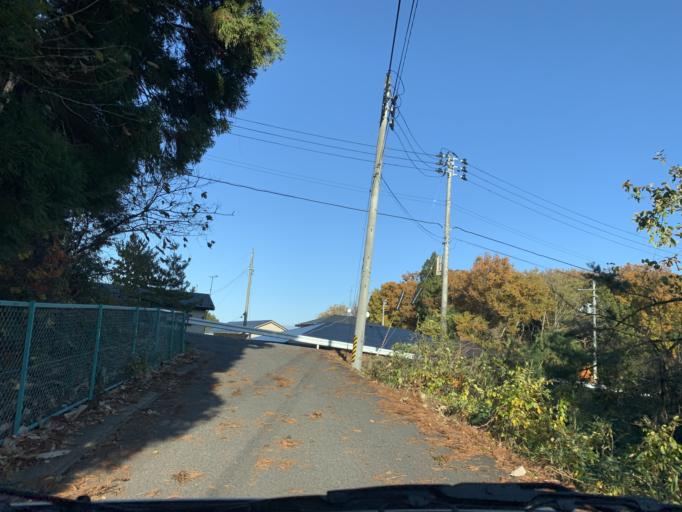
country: JP
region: Iwate
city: Kitakami
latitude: 39.2407
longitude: 141.0958
